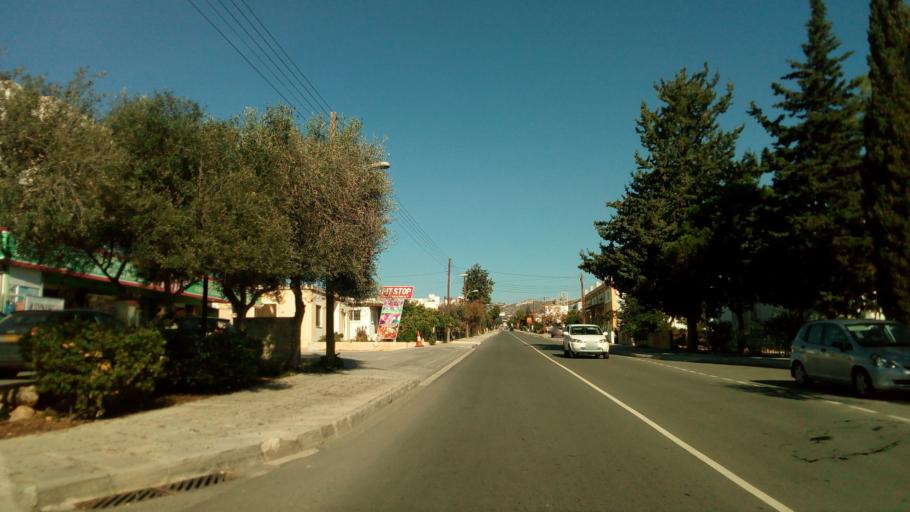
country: CY
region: Pafos
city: Paphos
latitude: 34.7915
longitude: 32.4434
